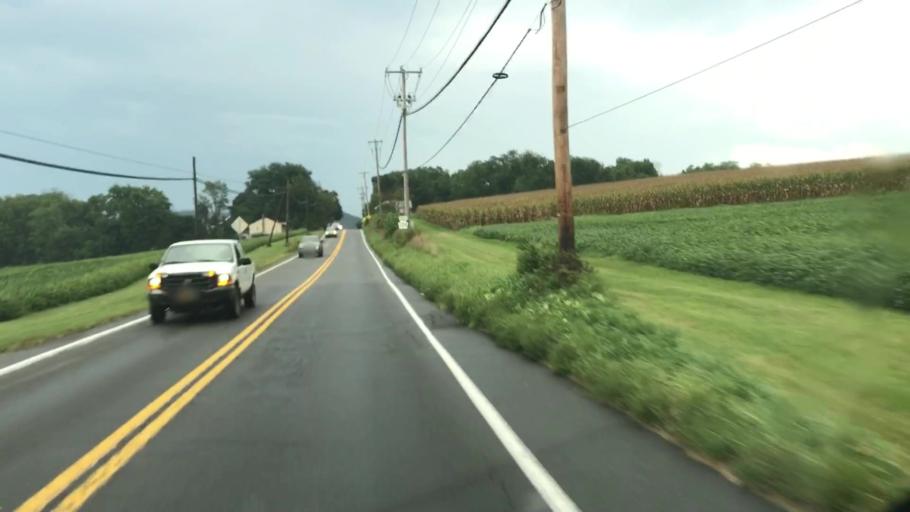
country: US
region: Pennsylvania
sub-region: Perry County
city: Duncannon
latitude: 40.3934
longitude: -77.0505
